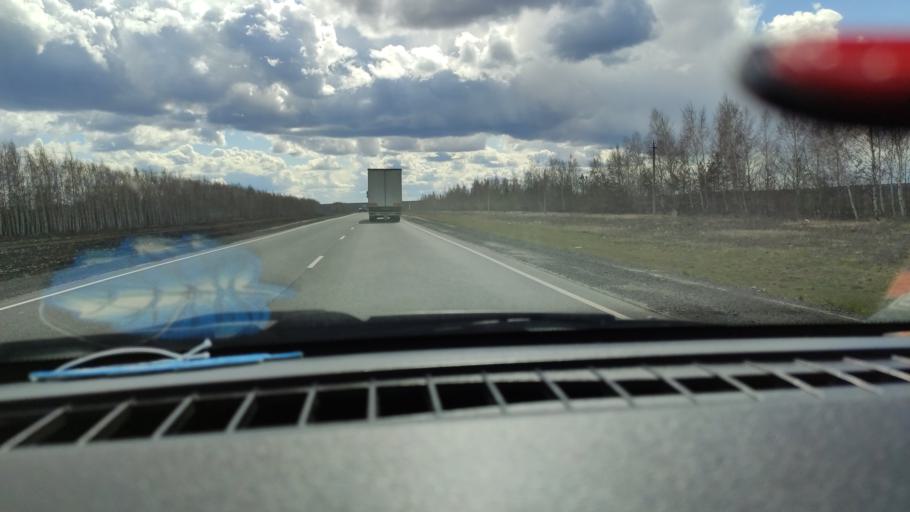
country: RU
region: Samara
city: Syzran'
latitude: 52.9880
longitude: 48.3191
